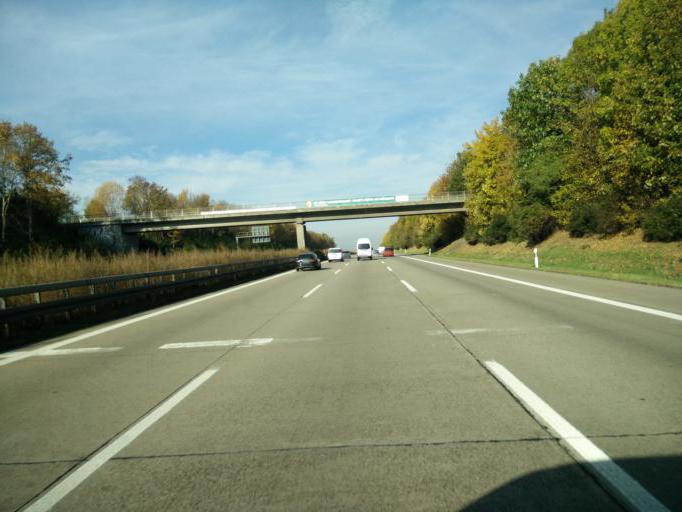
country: DE
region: Baden-Wuerttemberg
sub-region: Regierungsbezirk Stuttgart
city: Denkendorf
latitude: 48.6793
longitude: 9.3370
